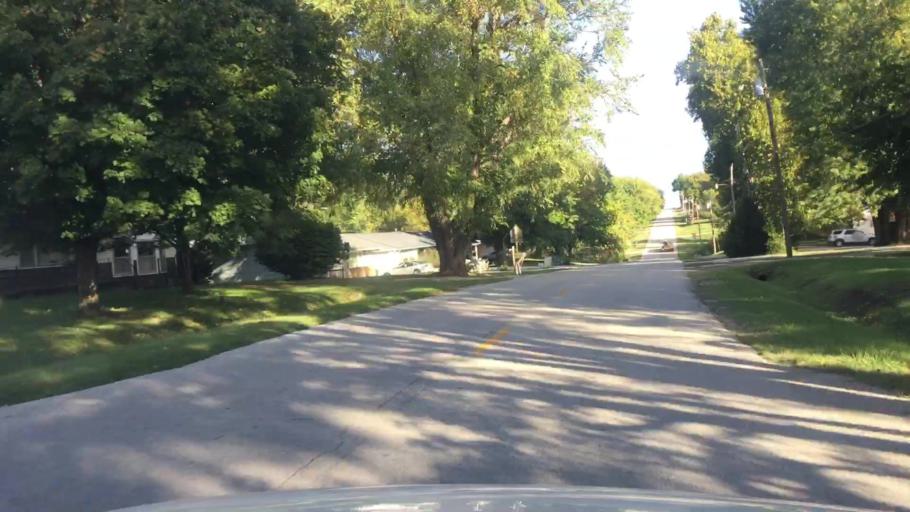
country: US
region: Missouri
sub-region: Howard County
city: New Franklin
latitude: 39.0190
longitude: -92.7448
